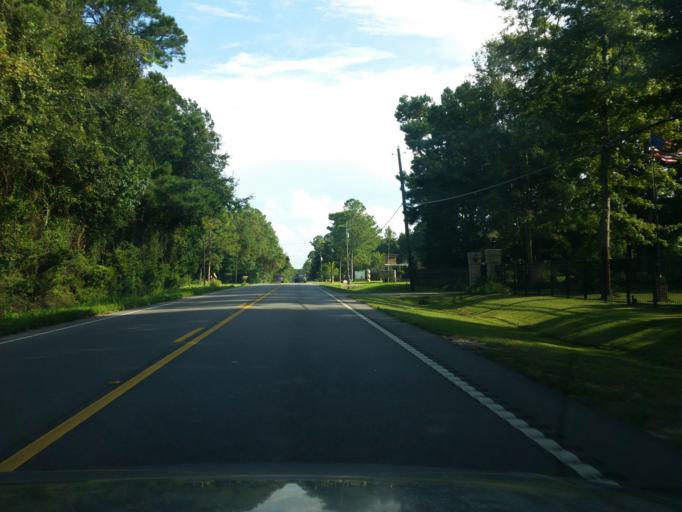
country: US
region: Alabama
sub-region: Mobile County
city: Theodore
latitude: 30.4360
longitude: -88.1094
